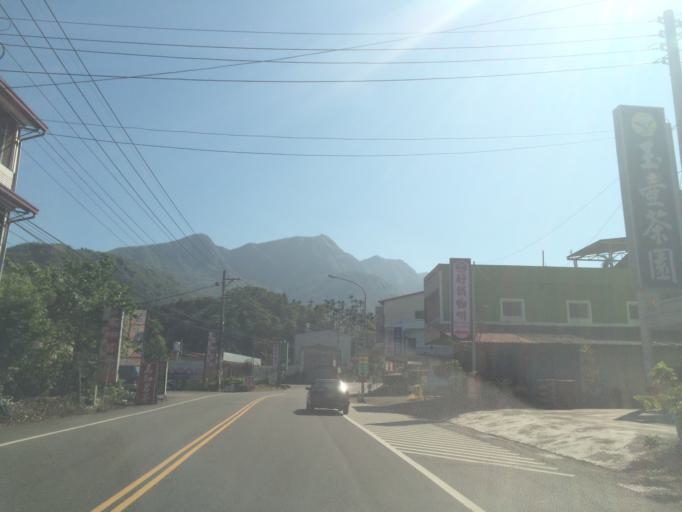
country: TW
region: Taiwan
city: Lugu
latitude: 23.7322
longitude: 120.7689
